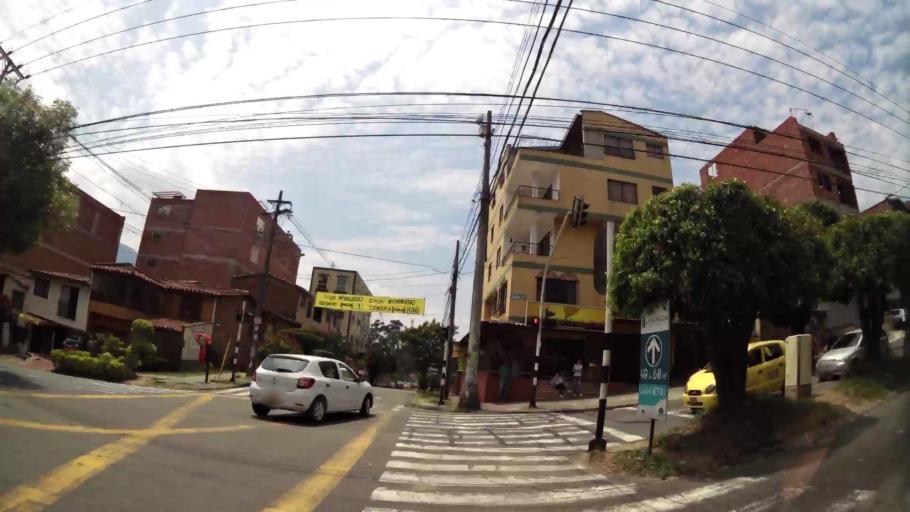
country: CO
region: Antioquia
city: Bello
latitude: 6.3141
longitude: -75.5636
